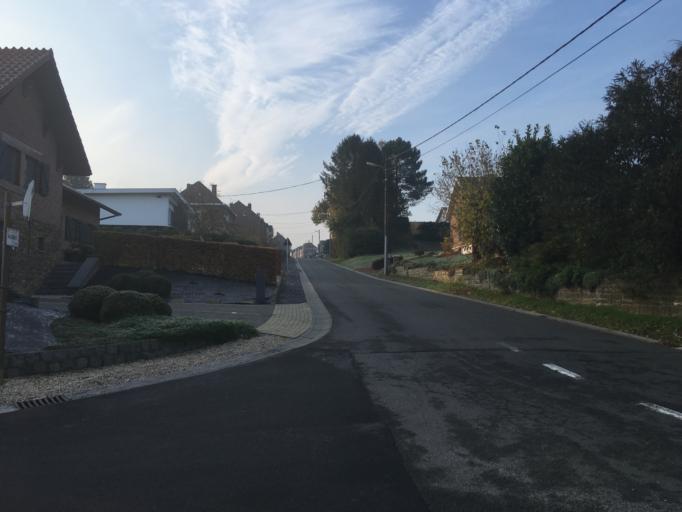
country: BE
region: Flanders
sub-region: Provincie Vlaams-Brabant
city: Beersel
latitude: 50.7266
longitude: 4.3067
